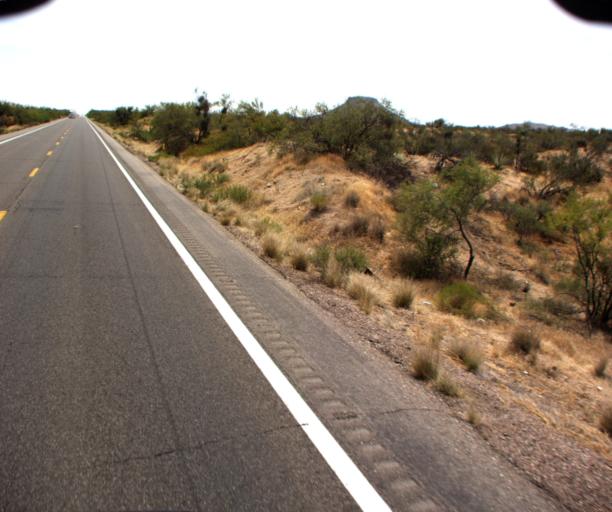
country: US
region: Arizona
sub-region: Gila County
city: San Carlos
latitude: 33.3374
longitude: -110.5906
